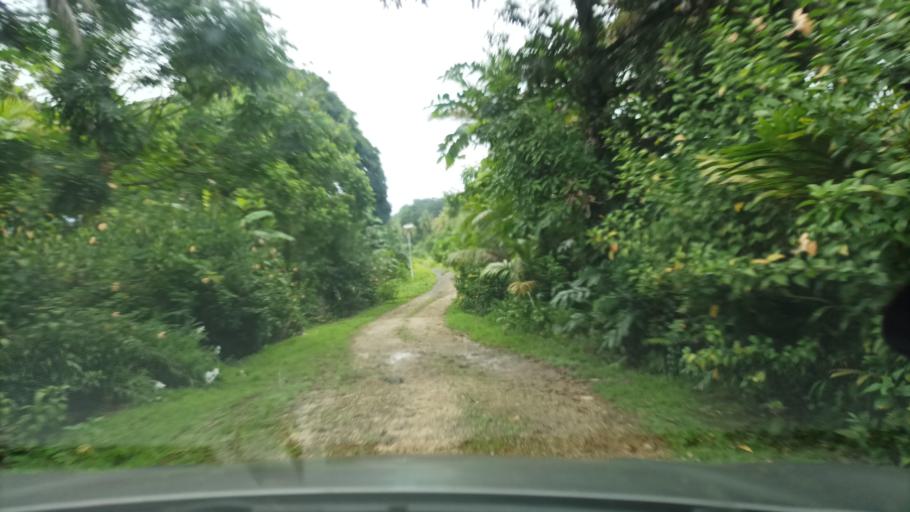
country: FM
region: Pohnpei
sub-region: Madolenihm Municipality
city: Madolenihm Municipality Government
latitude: 6.9120
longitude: 158.2870
